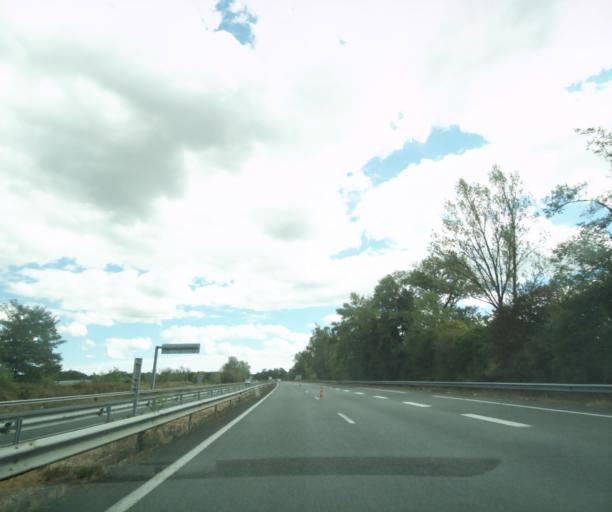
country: FR
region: Aquitaine
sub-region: Departement de la Gironde
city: Gironde-sur-Dropt
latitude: 44.5160
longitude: -0.0771
